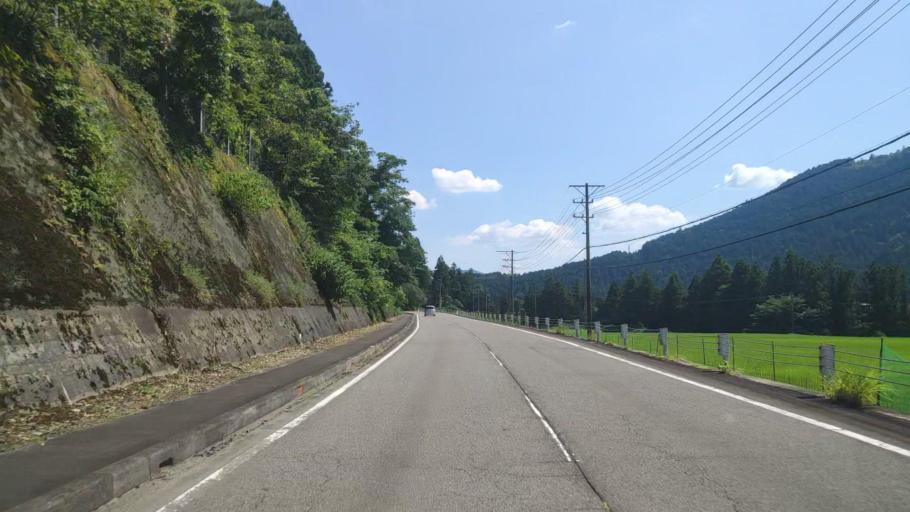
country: JP
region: Gifu
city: Godo
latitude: 35.5623
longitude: 136.6399
